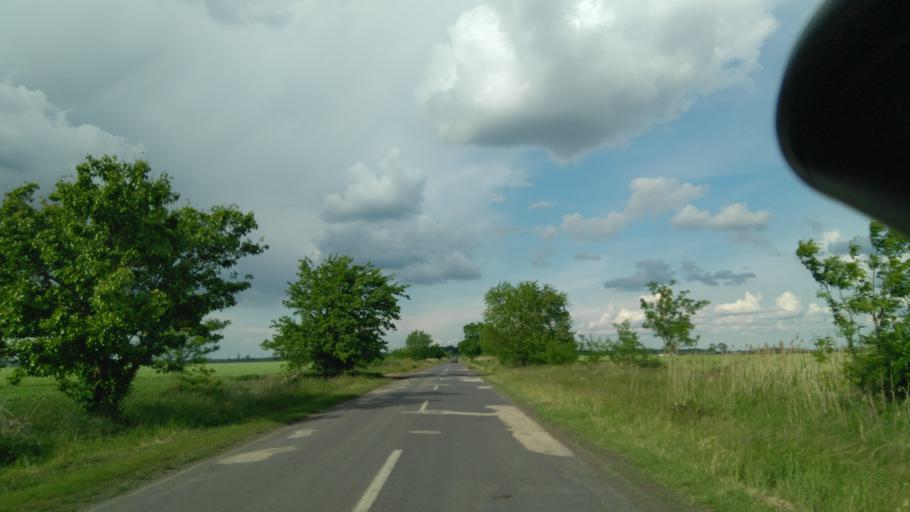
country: HU
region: Bekes
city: Dombegyhaz
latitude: 46.3237
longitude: 21.0904
